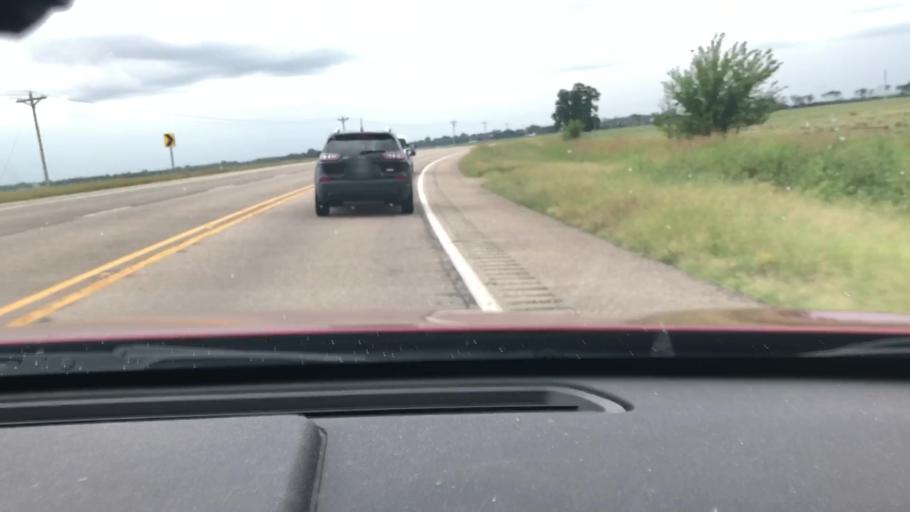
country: US
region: Arkansas
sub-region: Lafayette County
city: Lewisville
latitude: 33.3903
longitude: -93.7363
